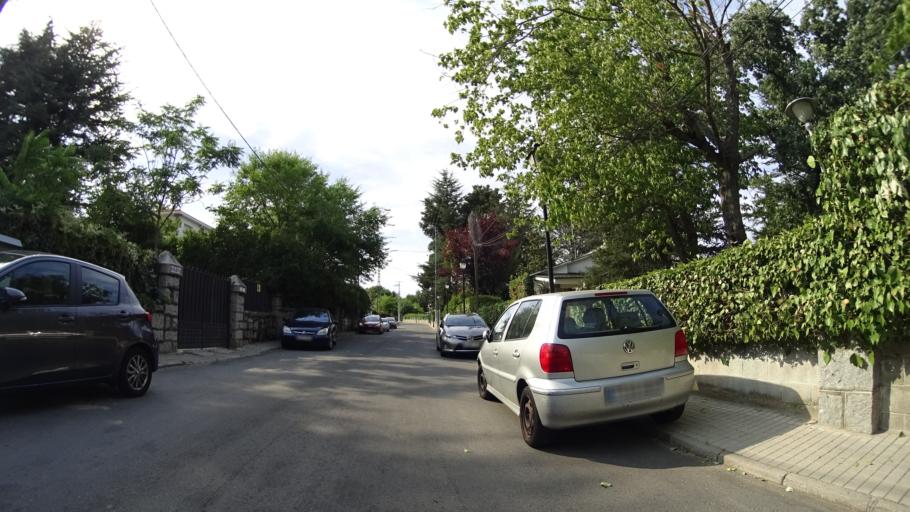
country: ES
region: Madrid
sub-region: Provincia de Madrid
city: Becerril de la Sierra
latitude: 40.7056
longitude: -3.9924
